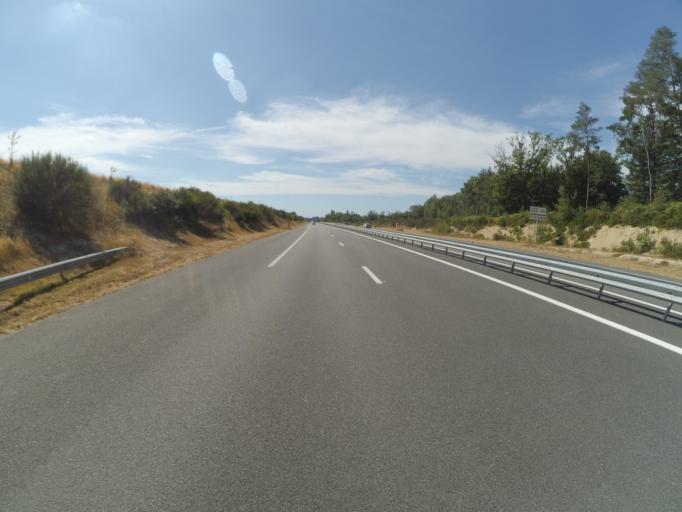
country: FR
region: Limousin
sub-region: Departement de la Haute-Vienne
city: Veyrac
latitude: 45.8873
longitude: 1.0725
